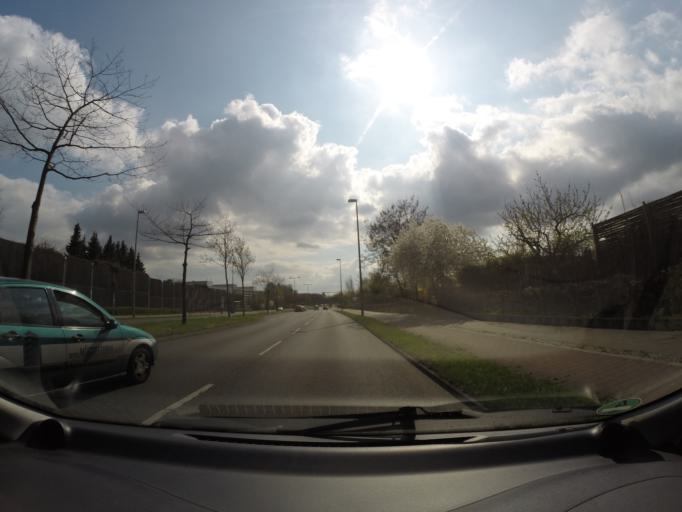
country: DE
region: Berlin
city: Kaulsdorf
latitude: 52.5343
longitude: 13.5868
